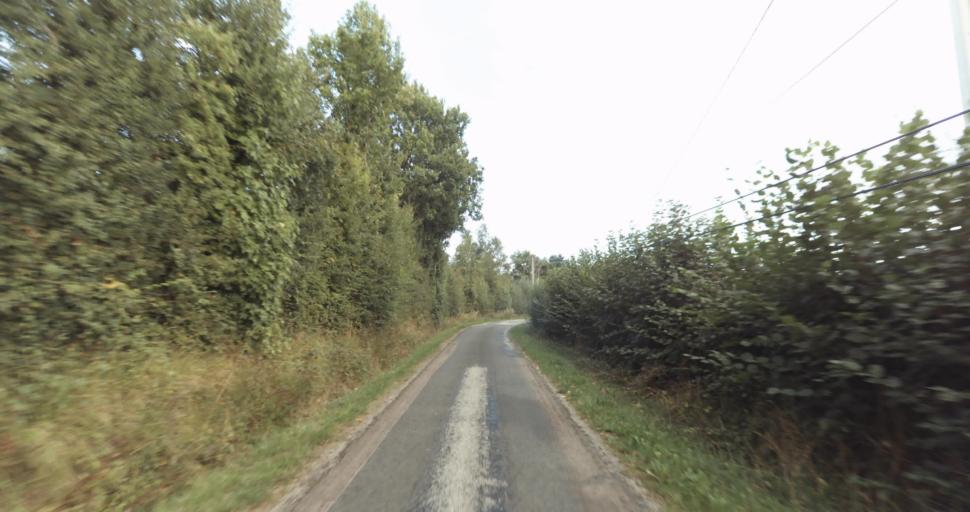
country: FR
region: Lower Normandy
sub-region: Departement de l'Orne
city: Gace
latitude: 48.7672
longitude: 0.3544
